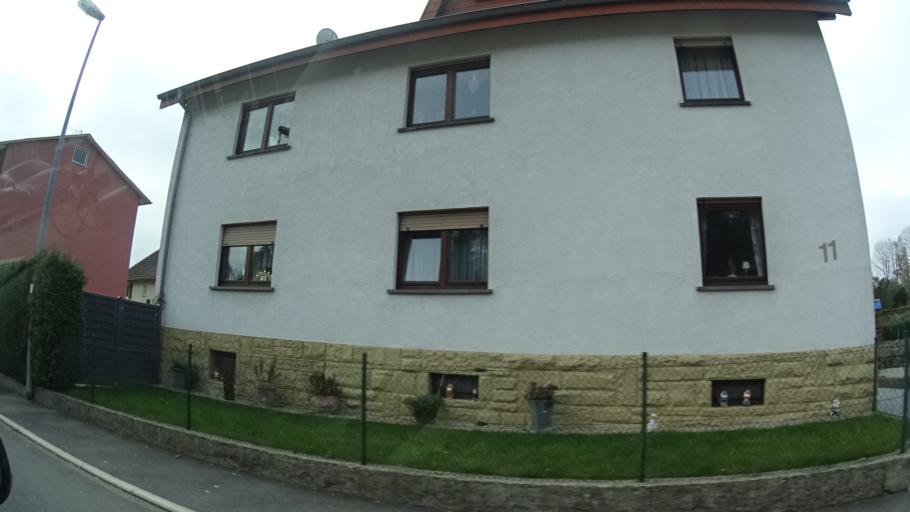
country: DE
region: Baden-Wuerttemberg
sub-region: Karlsruhe Region
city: Bammental
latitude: 49.3719
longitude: 8.7720
